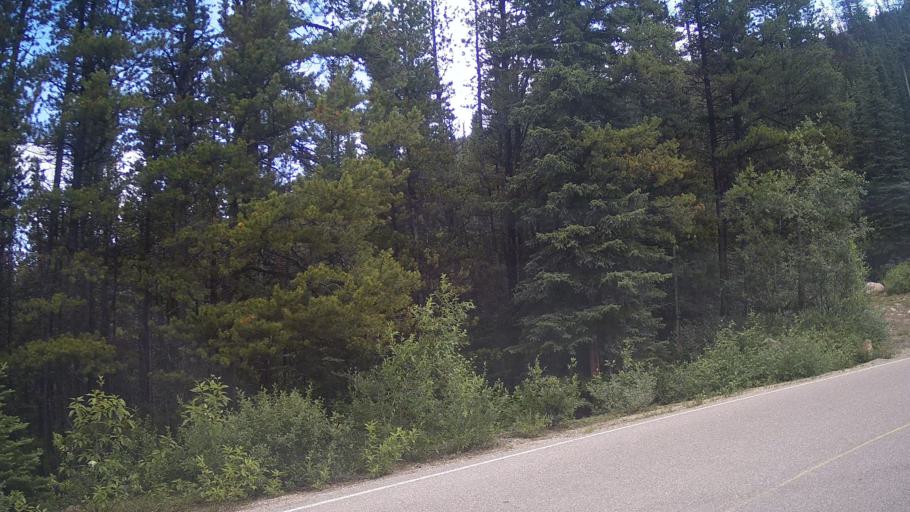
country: CA
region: Alberta
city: Jasper Park Lodge
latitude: 52.7310
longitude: -118.0490
